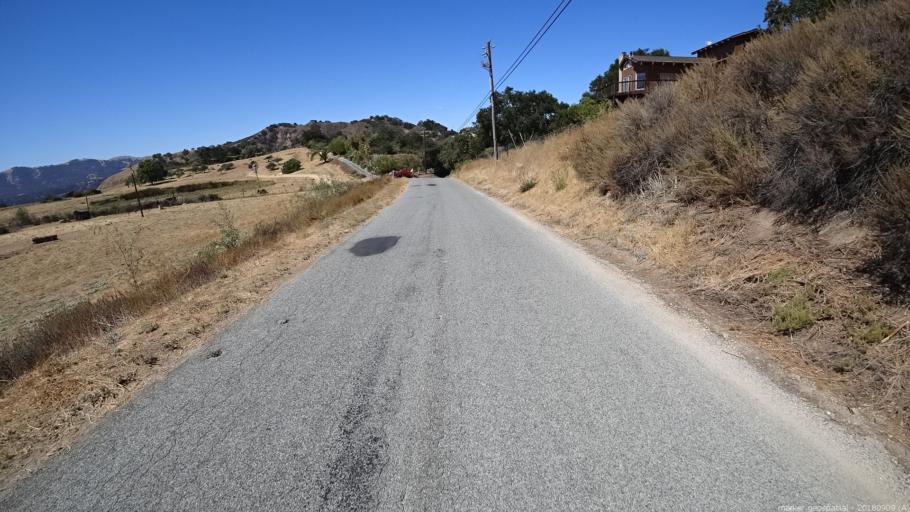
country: US
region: California
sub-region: Monterey County
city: Carmel Valley Village
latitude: 36.5418
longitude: -121.6610
